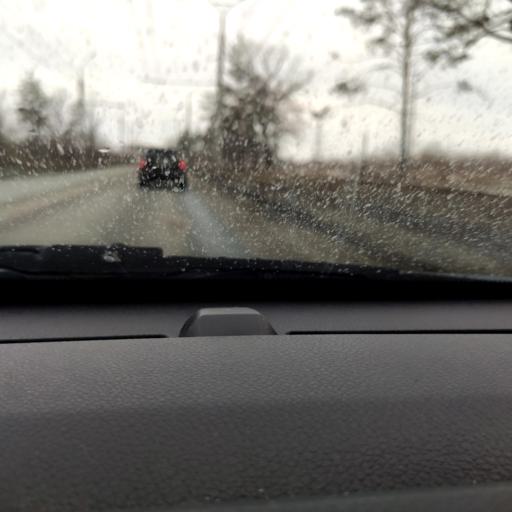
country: RU
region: Samara
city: Tol'yatti
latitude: 53.4848
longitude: 49.3759
